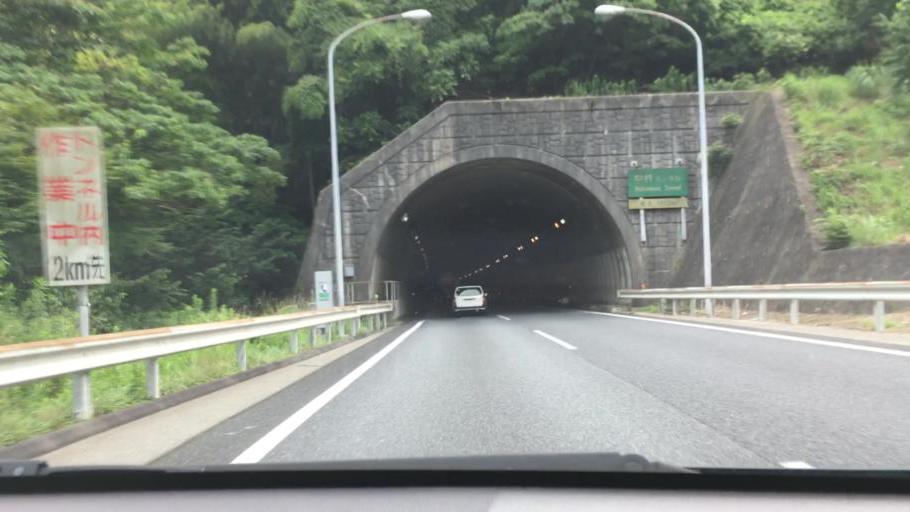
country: JP
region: Yamaguchi
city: Tokuyama
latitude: 34.0756
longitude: 131.7156
